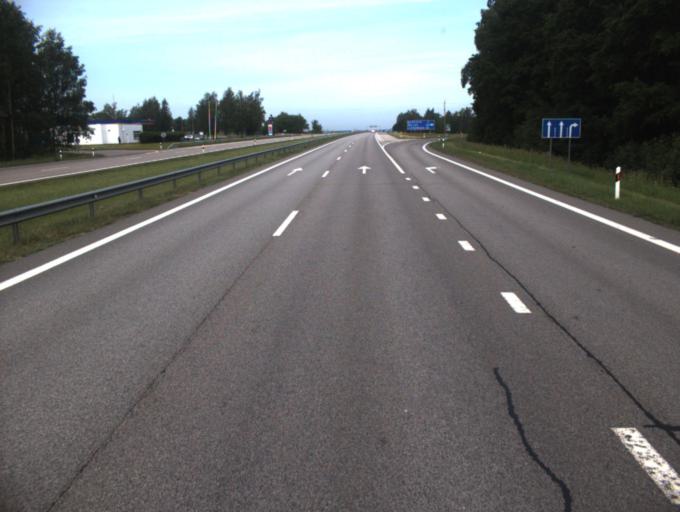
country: LT
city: Raseiniai
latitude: 55.3356
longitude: 23.1048
